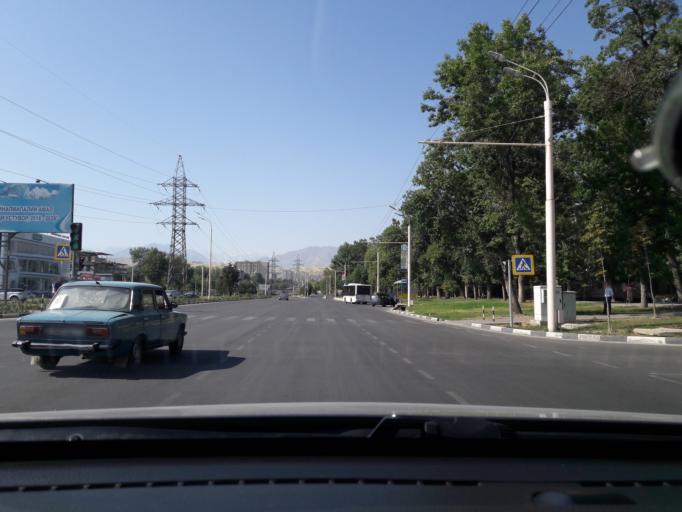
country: TJ
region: Dushanbe
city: Dushanbe
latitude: 38.5615
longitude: 68.7415
